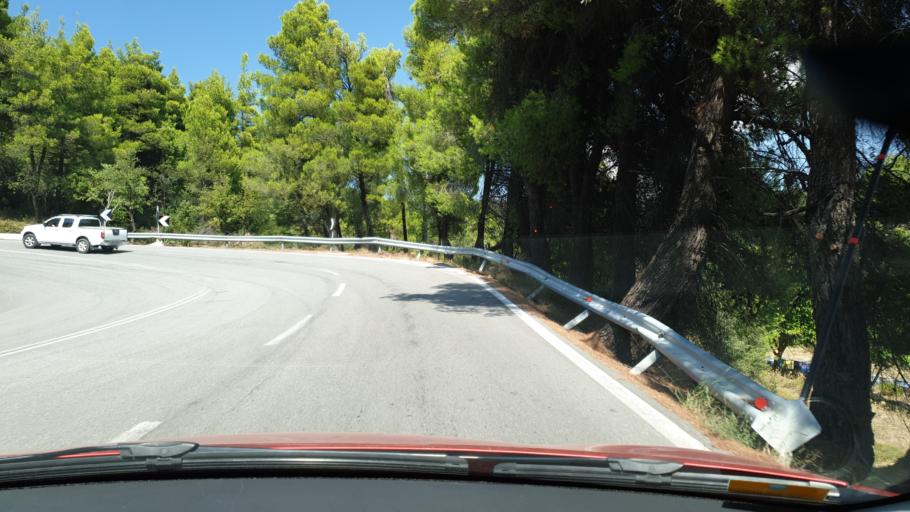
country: GR
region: Central Greece
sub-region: Nomos Evvoias
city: Politika
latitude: 38.6439
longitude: 23.5654
